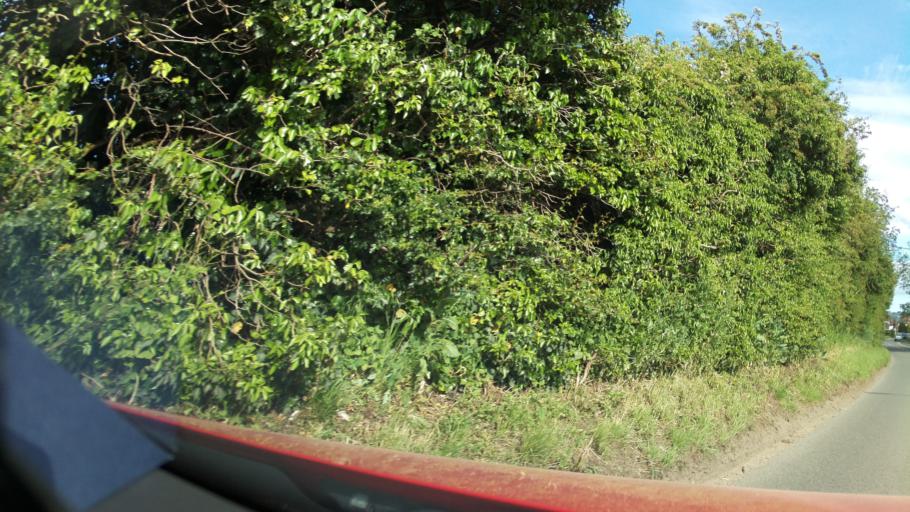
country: GB
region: England
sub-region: Worcestershire
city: South Littleton
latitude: 52.0937
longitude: -1.8652
